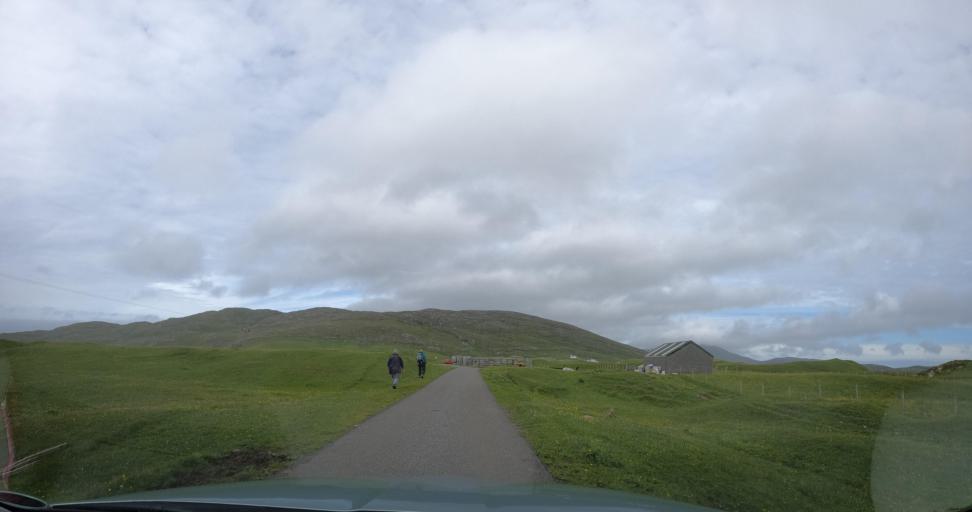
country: GB
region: Scotland
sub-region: Eilean Siar
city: Barra
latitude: 56.9207
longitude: -7.5377
